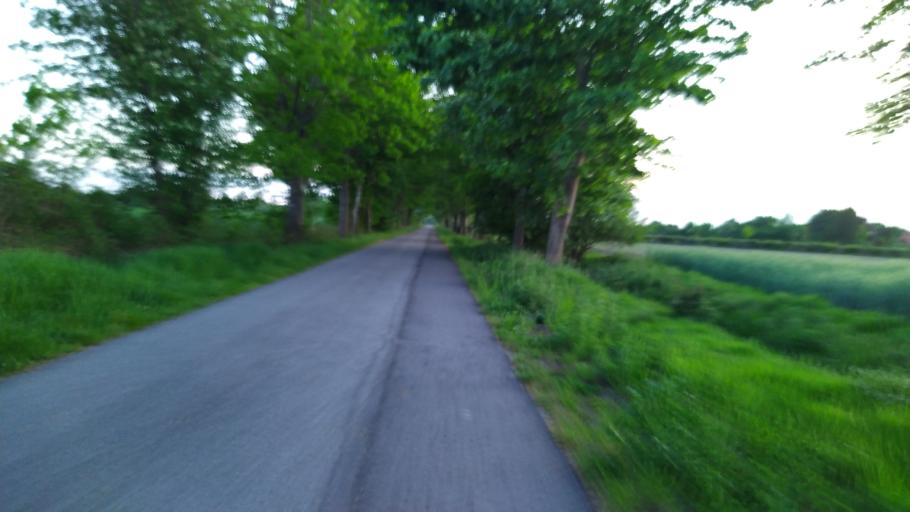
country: DE
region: Lower Saxony
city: Harsefeld
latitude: 53.4798
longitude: 9.4829
